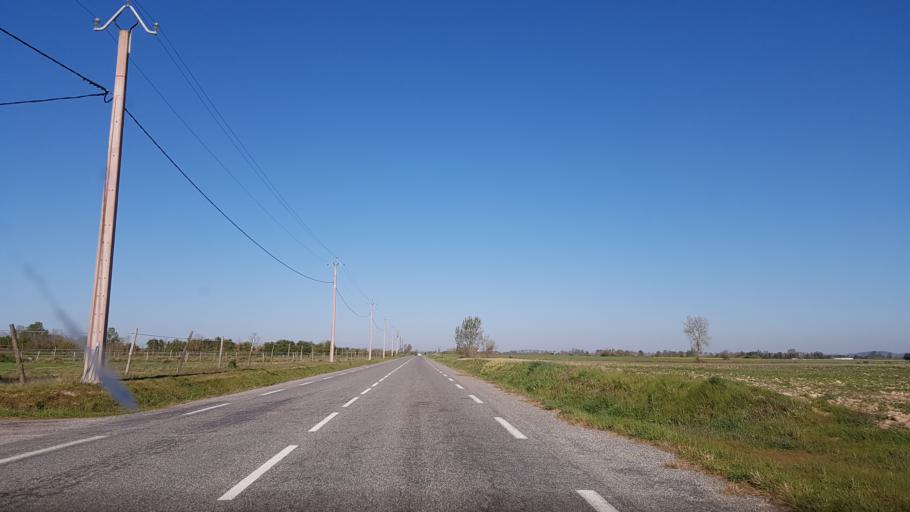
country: FR
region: Midi-Pyrenees
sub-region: Departement de l'Ariege
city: Mazeres
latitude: 43.2279
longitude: 1.6767
